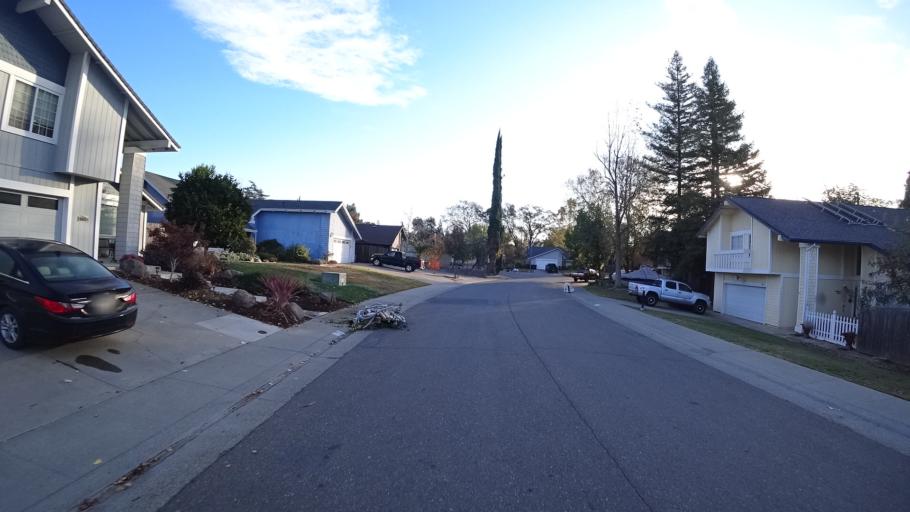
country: US
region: California
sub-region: Sacramento County
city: Antelope
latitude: 38.6766
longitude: -121.3081
